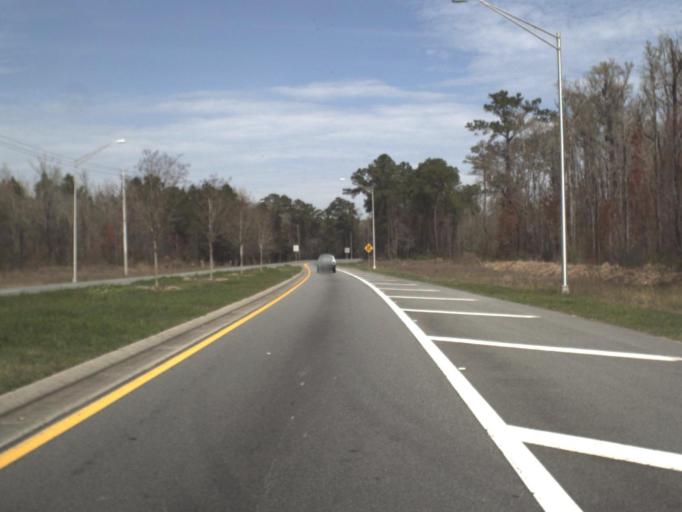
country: US
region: Florida
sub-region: Gadsden County
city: Midway
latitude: 30.4854
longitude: -84.3631
